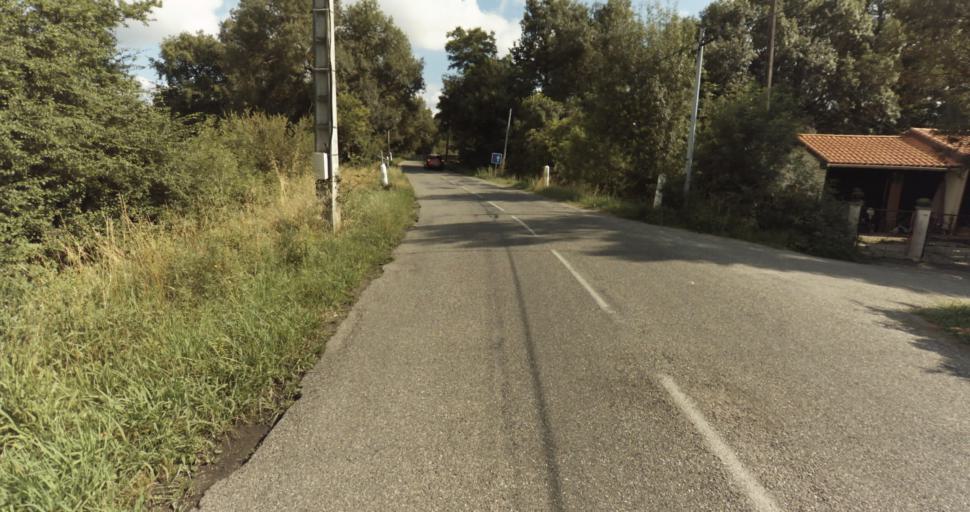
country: FR
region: Midi-Pyrenees
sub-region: Departement de la Haute-Garonne
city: Fonsorbes
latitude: 43.5632
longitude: 1.2332
